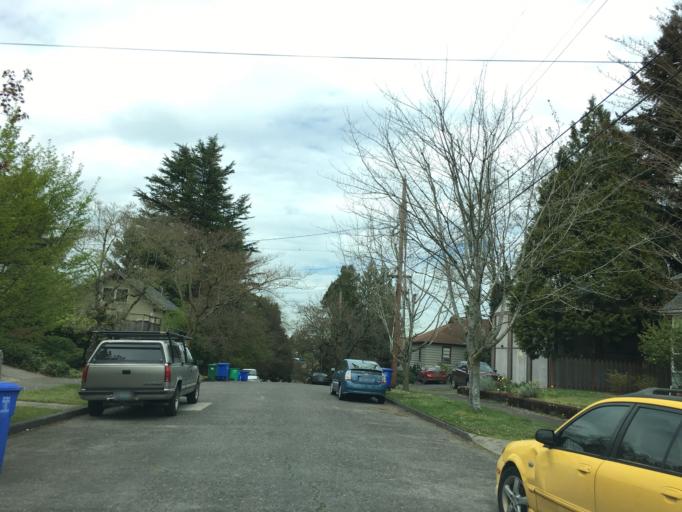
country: US
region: Oregon
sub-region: Multnomah County
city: Lents
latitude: 45.5251
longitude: -122.5986
